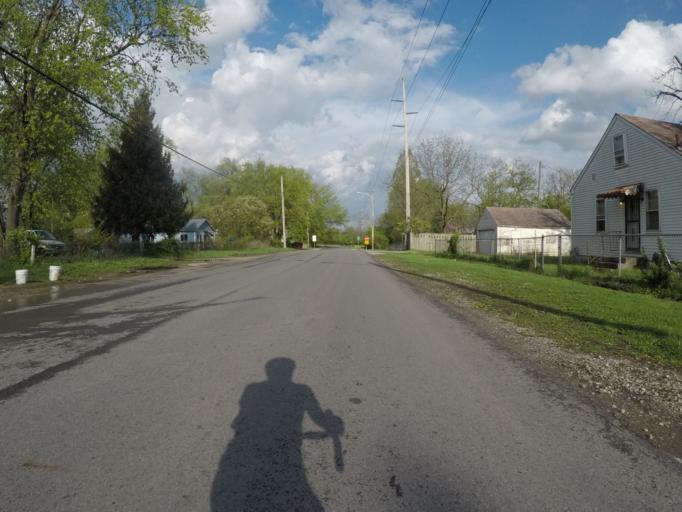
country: US
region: Ohio
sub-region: Franklin County
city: Bexley
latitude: 40.0131
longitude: -82.9552
